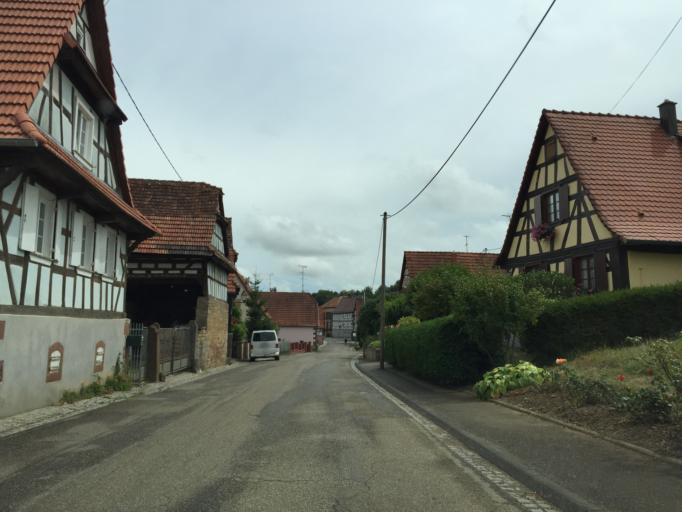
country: FR
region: Alsace
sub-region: Departement du Bas-Rhin
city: Soultz-sous-Forets
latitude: 48.9783
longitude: 7.8780
